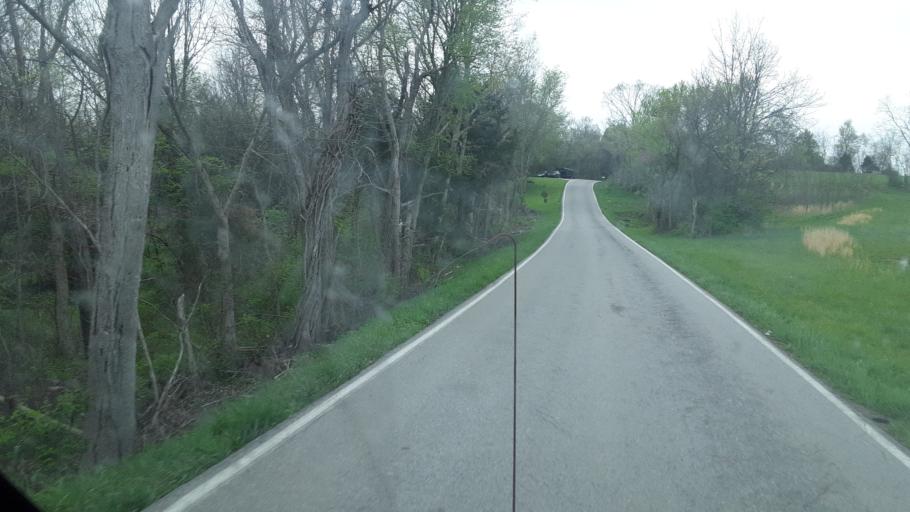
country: US
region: Kentucky
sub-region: Owen County
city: Owenton
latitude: 38.6593
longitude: -84.7722
